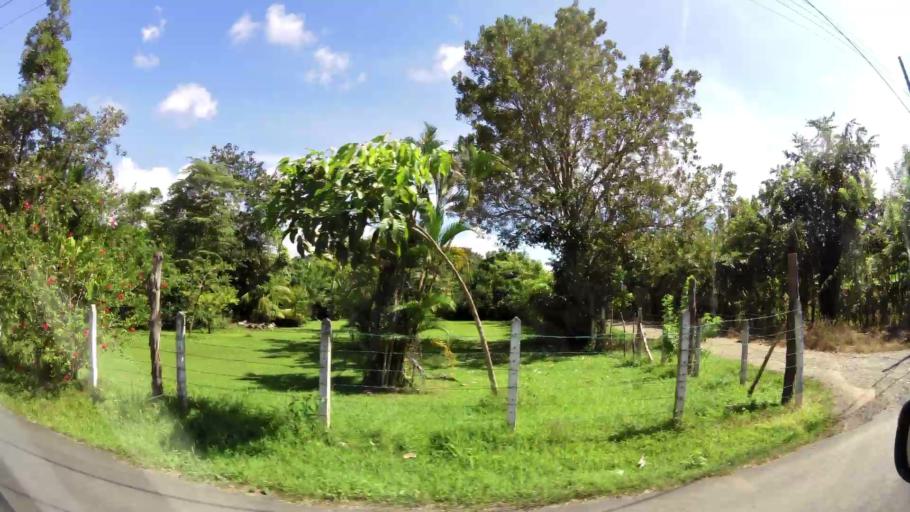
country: CR
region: Puntarenas
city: Quepos
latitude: 9.3273
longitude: -83.9575
